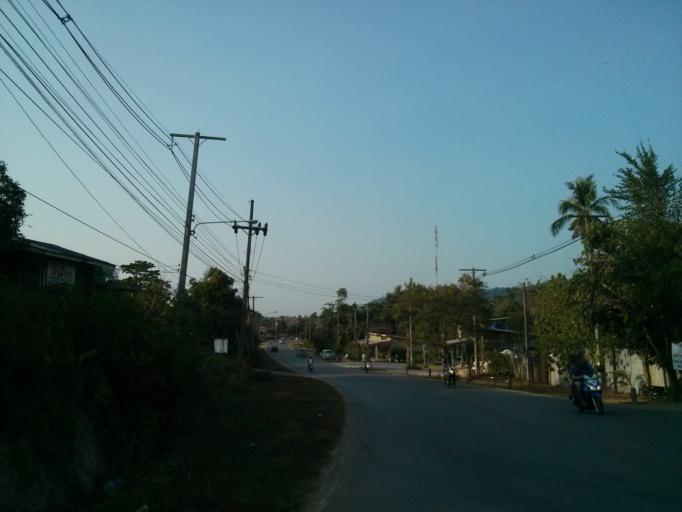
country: TH
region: Krabi
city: Saladan
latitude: 7.5879
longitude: 99.0356
